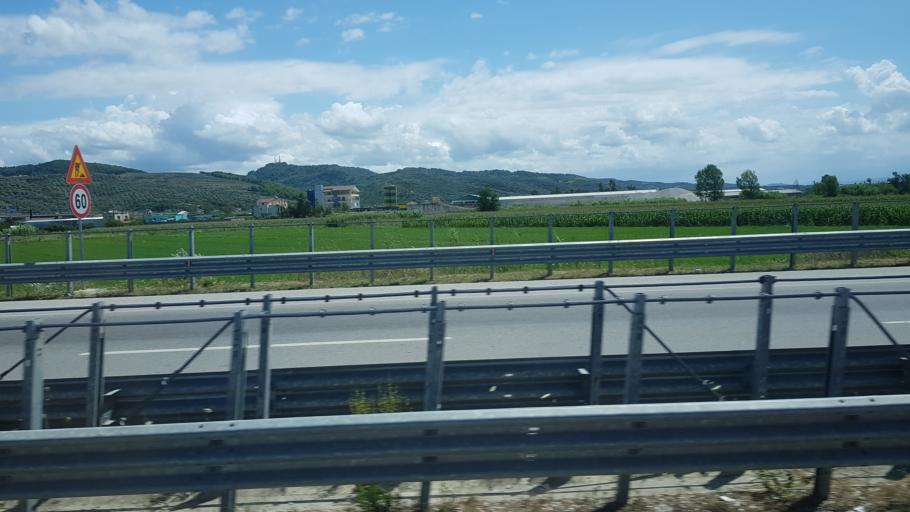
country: AL
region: Fier
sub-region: Rrethi i Fierit
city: Levan
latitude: 40.6683
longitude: 19.4782
